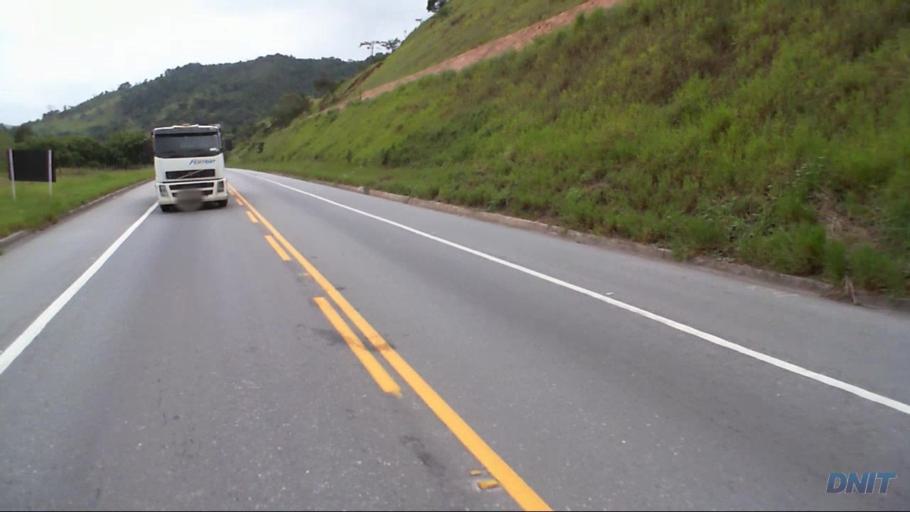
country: BR
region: Minas Gerais
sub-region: Nova Era
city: Nova Era
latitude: -19.7189
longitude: -43.0037
